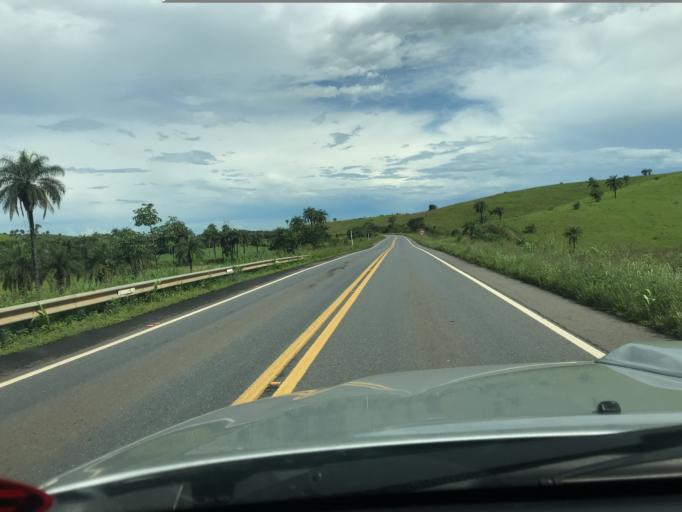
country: BR
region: Minas Gerais
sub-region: Bambui
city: Bambui
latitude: -19.8347
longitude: -46.0030
